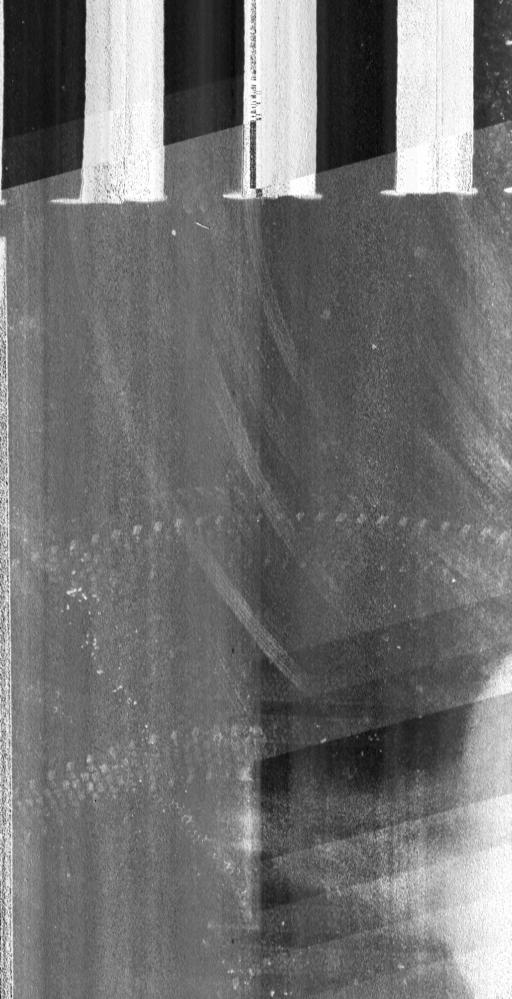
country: US
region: Vermont
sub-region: Chittenden County
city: Burlington
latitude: 44.3744
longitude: -73.2257
